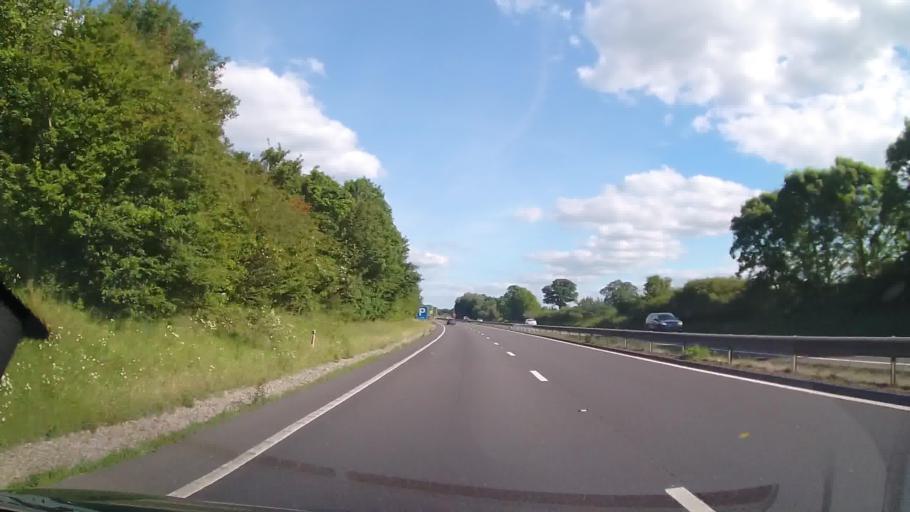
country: GB
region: England
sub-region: Shropshire
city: Great Hanwood
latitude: 52.7083
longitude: -2.8161
